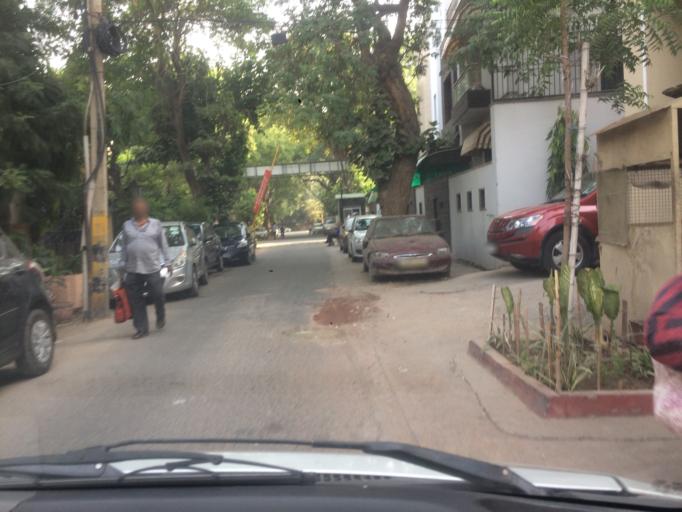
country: IN
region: NCT
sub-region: New Delhi
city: New Delhi
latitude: 28.5536
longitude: 77.2329
